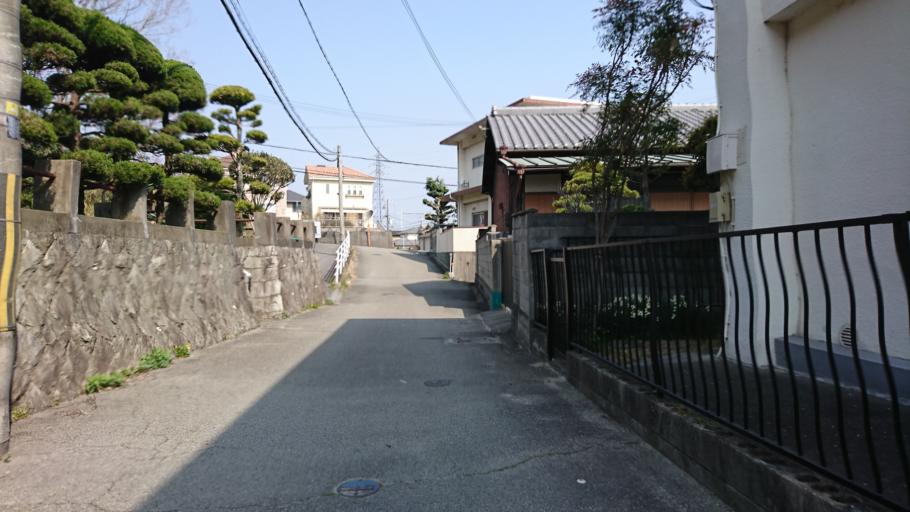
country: JP
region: Hyogo
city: Shirahamacho-usazakiminami
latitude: 34.7939
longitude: 134.7614
